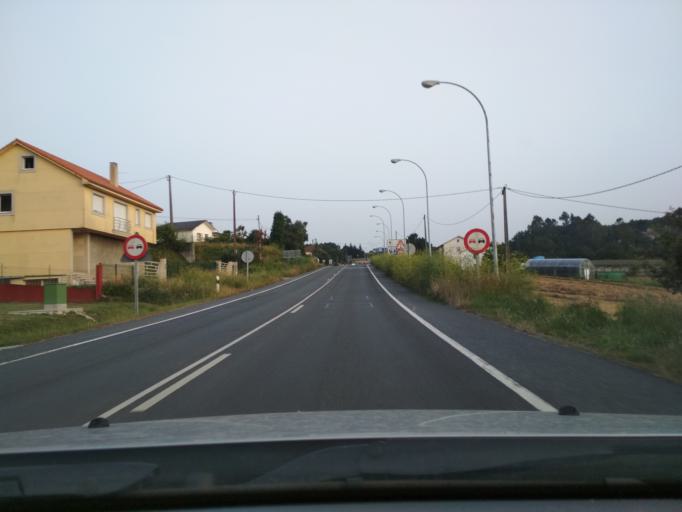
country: ES
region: Galicia
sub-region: Provincia da Coruna
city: Cambre
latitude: 43.2787
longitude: -8.3655
